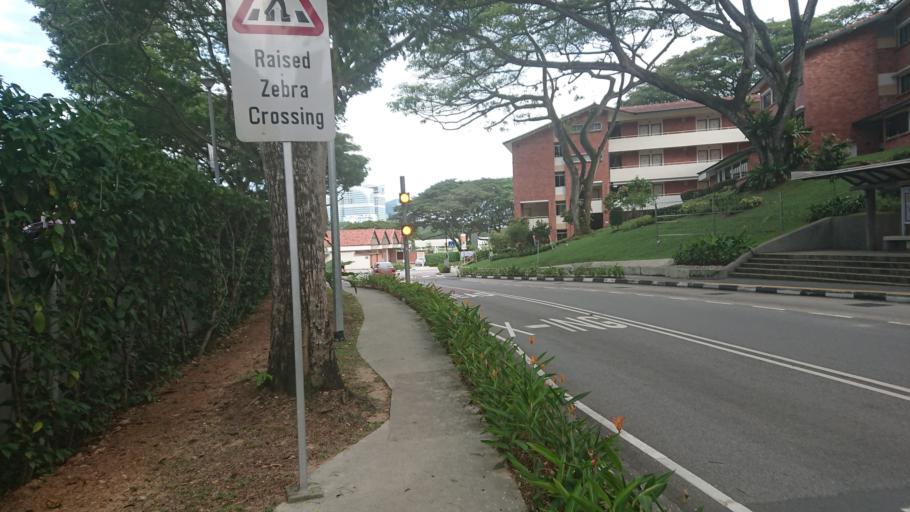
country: SG
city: Singapore
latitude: 1.2990
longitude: 103.7755
